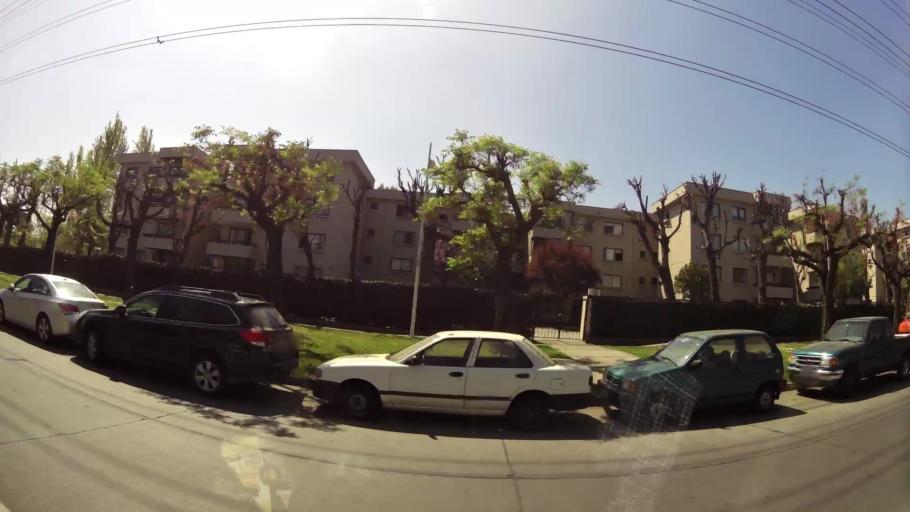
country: CL
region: Santiago Metropolitan
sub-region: Provincia de Santiago
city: Villa Presidente Frei, Nunoa, Santiago, Chile
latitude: -33.4265
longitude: -70.5440
